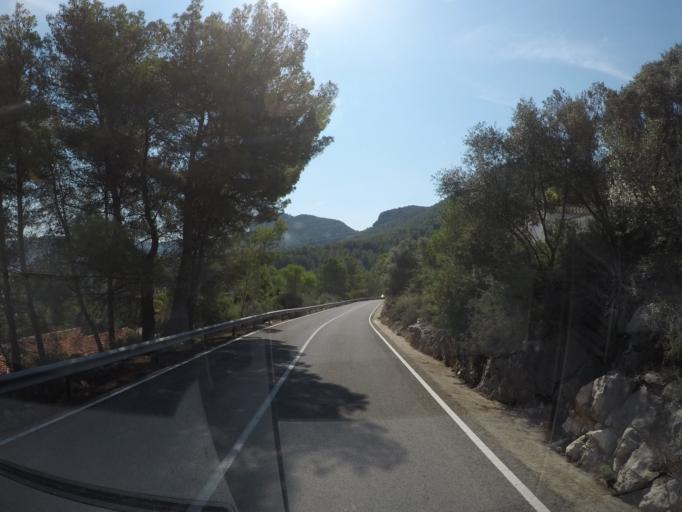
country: ES
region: Valencia
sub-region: Provincia de Alicante
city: Orba
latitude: 38.7822
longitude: -0.0798
